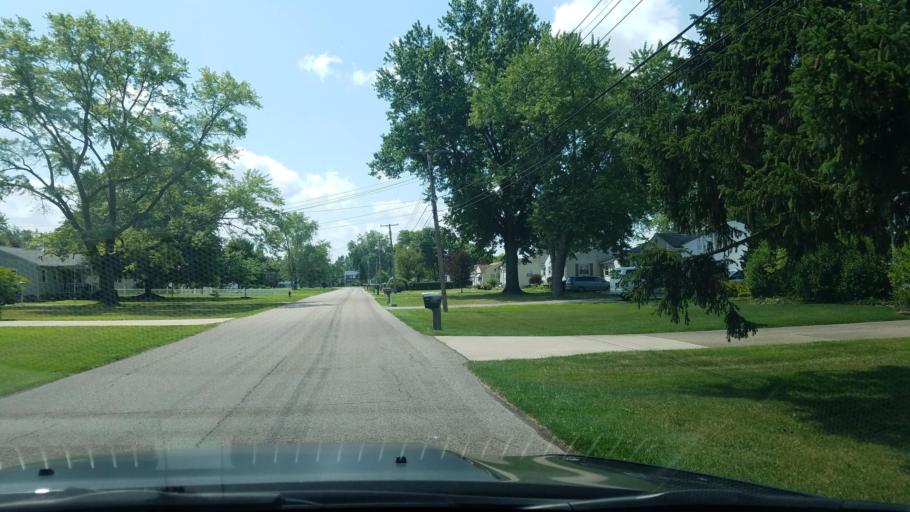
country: US
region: Ohio
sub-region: Trumbull County
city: Champion Heights
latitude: 41.3113
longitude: -80.8572
